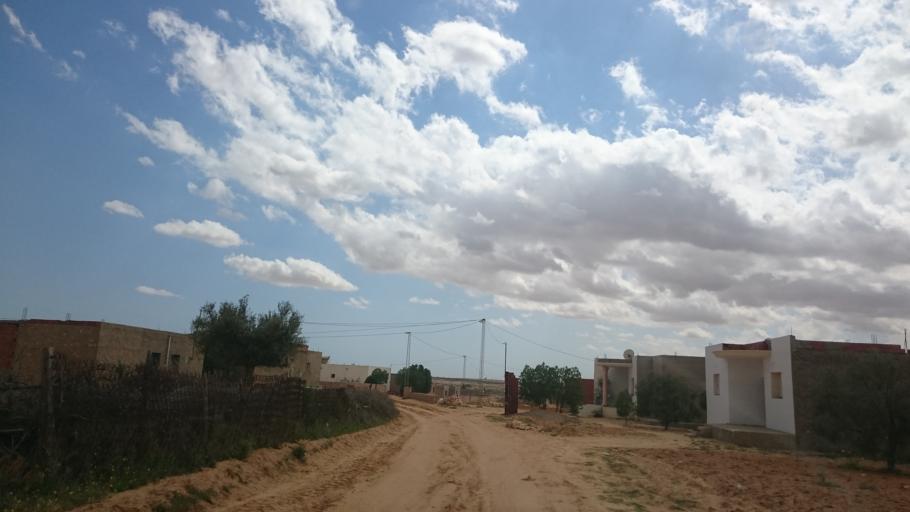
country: TN
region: Safaqis
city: Sfax
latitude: 34.7479
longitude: 10.4860
